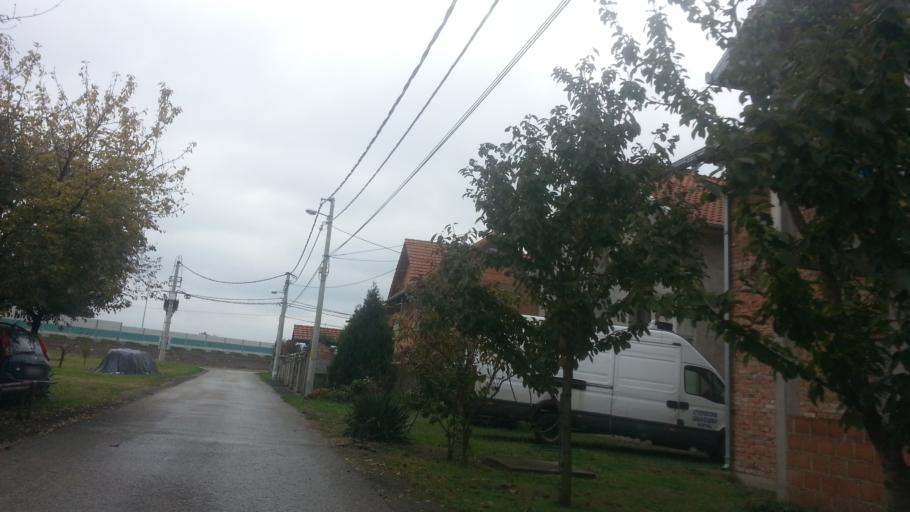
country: RS
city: Novi Banovci
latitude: 44.8984
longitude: 20.2993
